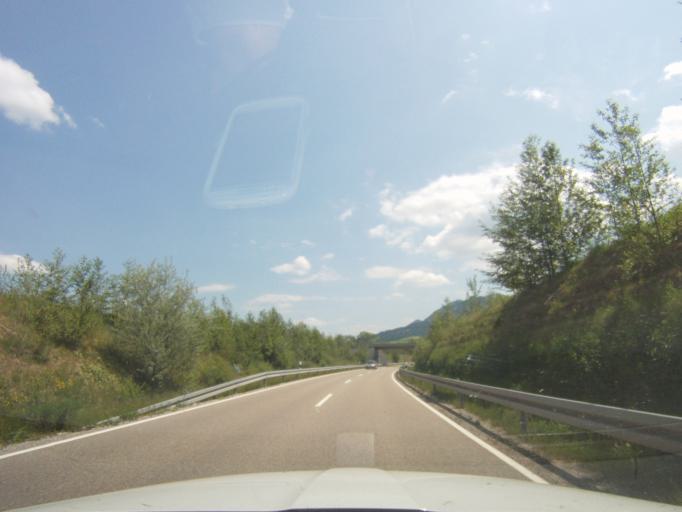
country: DE
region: Bavaria
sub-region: Swabia
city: Wertach
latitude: 47.5977
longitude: 10.4060
